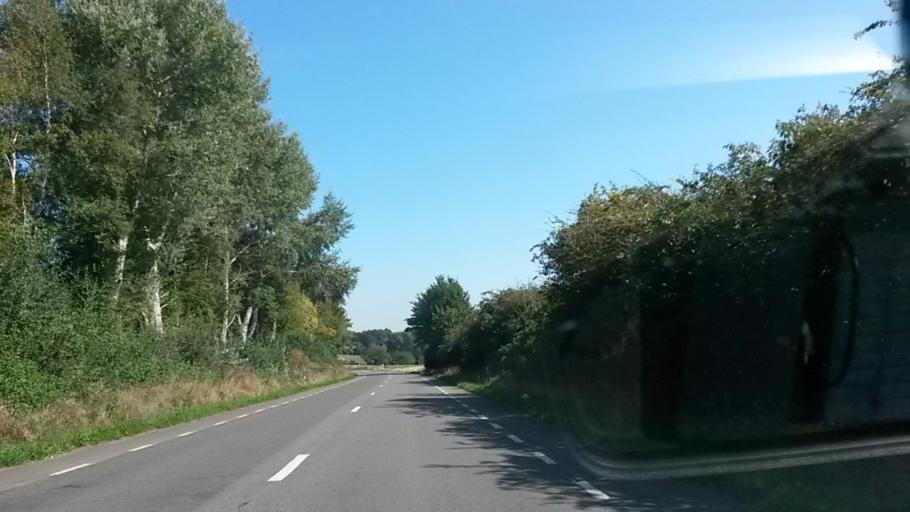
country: BE
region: Wallonia
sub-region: Province du Hainaut
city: Merbes-le-Chateau
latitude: 50.3166
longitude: 4.1467
